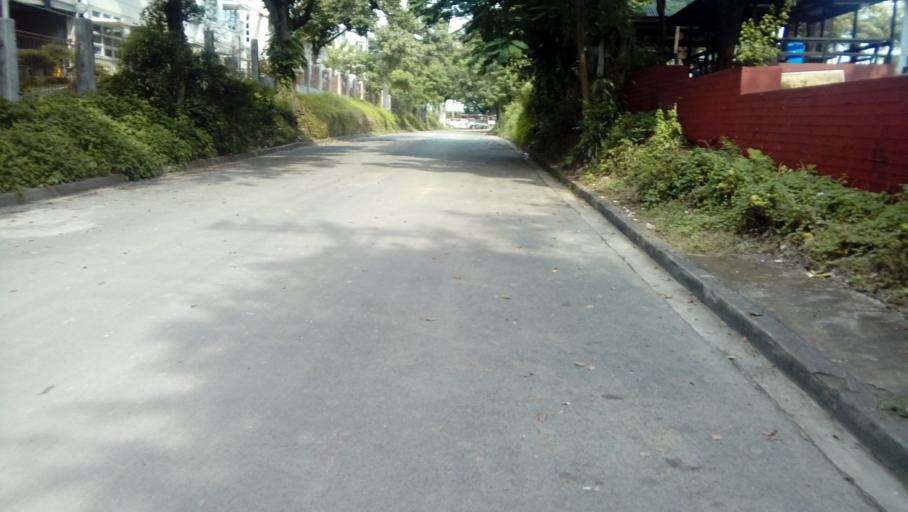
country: PH
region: Metro Manila
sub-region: Quezon City
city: Quezon City
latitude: 14.6525
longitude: 121.0729
